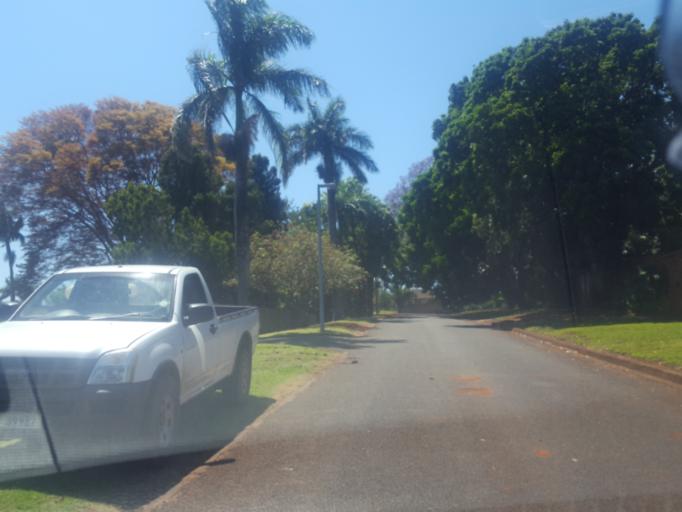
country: ZA
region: KwaZulu-Natal
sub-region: uThungulu District Municipality
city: Empangeni
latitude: -28.7486
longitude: 31.9038
